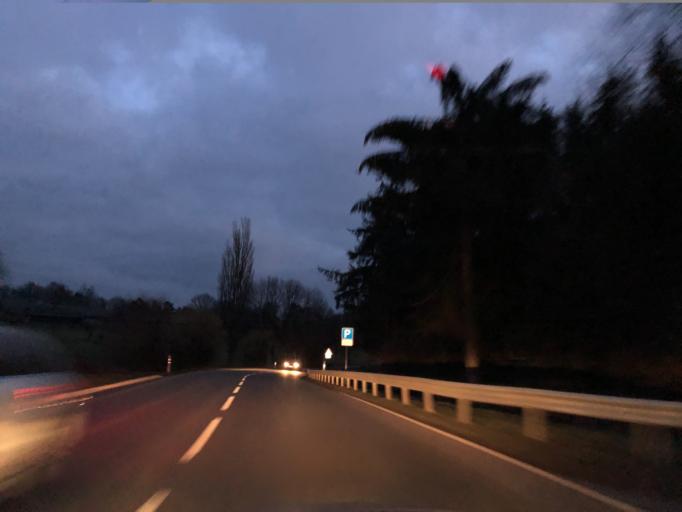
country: DE
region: Rheinland-Pfalz
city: Singhofen
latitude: 50.2958
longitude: 7.8181
